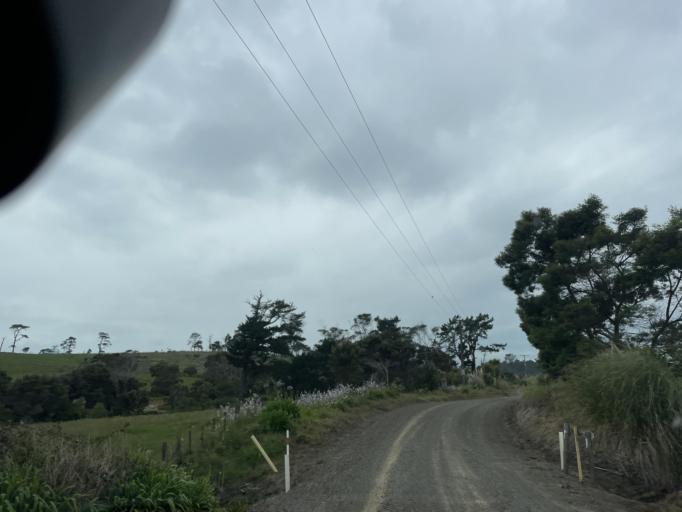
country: NZ
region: Auckland
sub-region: Auckland
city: Wellsford
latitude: -36.2551
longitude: 174.2312
